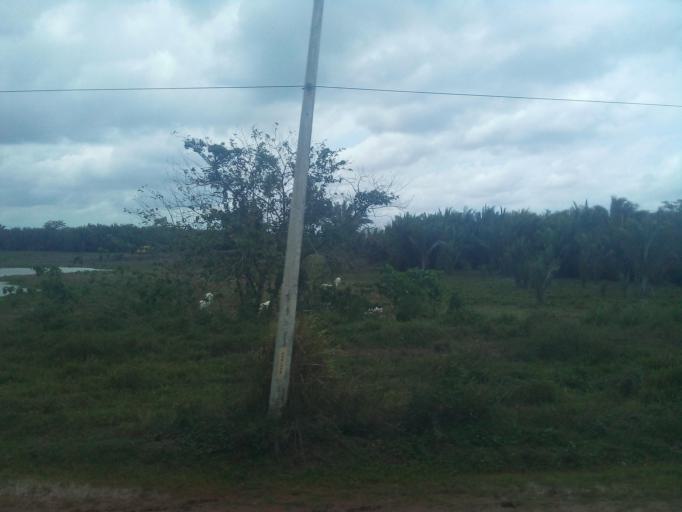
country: BR
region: Maranhao
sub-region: Pindare Mirim
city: Pindare Mirim
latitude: -3.6718
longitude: -45.3001
